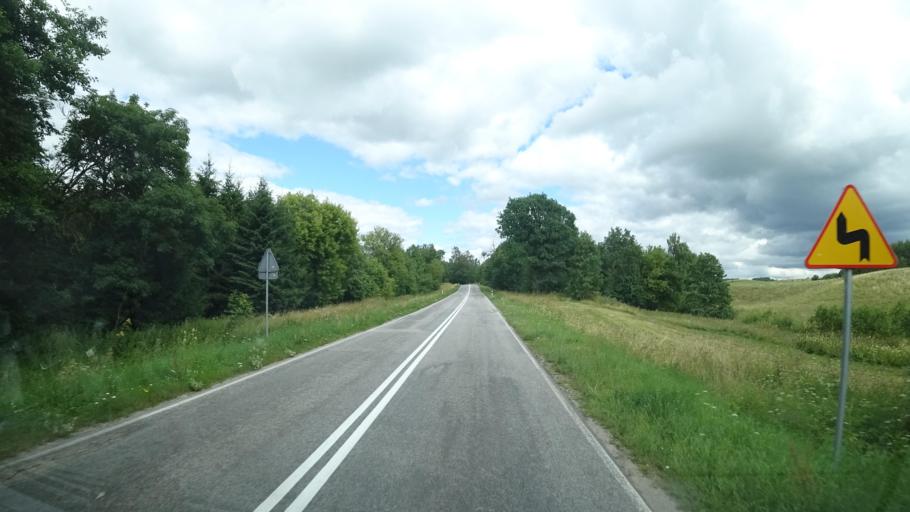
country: PL
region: Warmian-Masurian Voivodeship
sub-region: Powiat goldapski
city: Goldap
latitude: 54.2155
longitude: 22.2222
